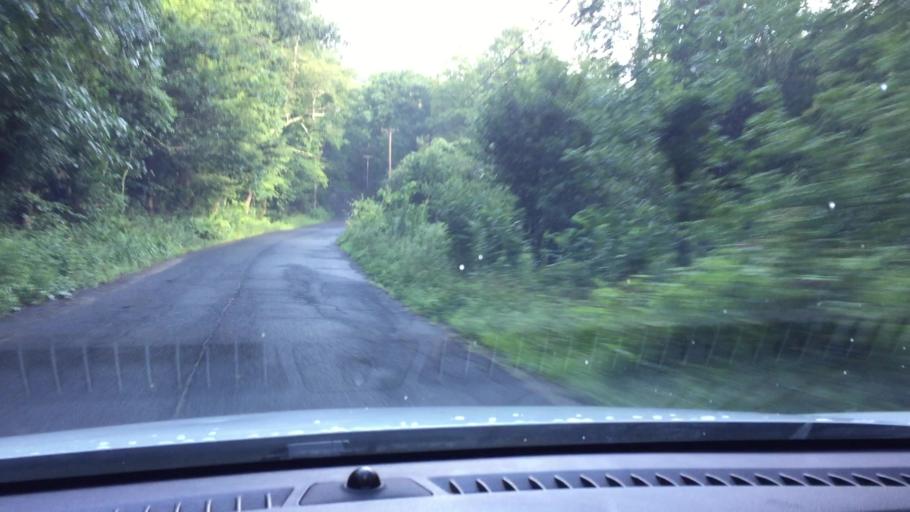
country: US
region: Massachusetts
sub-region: Hampshire County
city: Chesterfield
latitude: 42.3250
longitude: -72.9287
